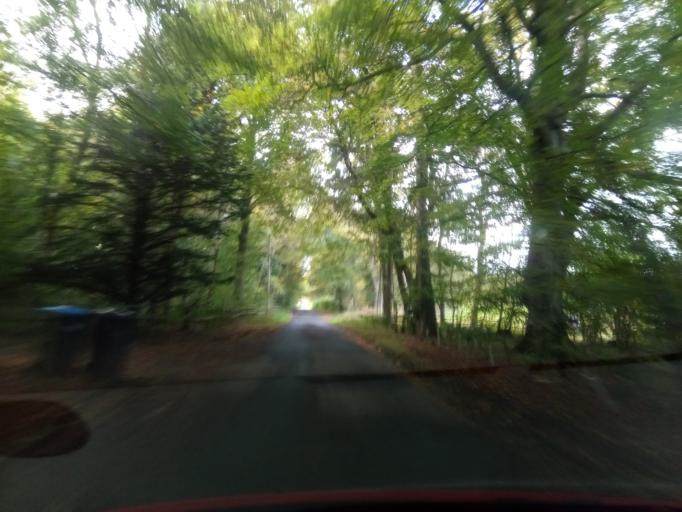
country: GB
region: Scotland
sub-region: The Scottish Borders
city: Galashiels
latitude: 55.6683
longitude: -2.8161
